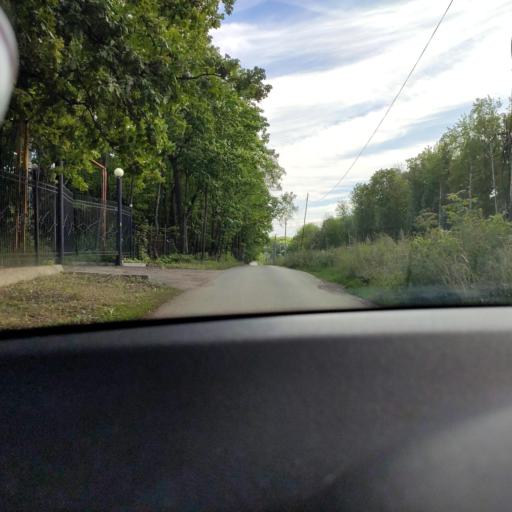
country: RU
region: Samara
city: Novosemeykino
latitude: 53.3501
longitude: 50.2443
